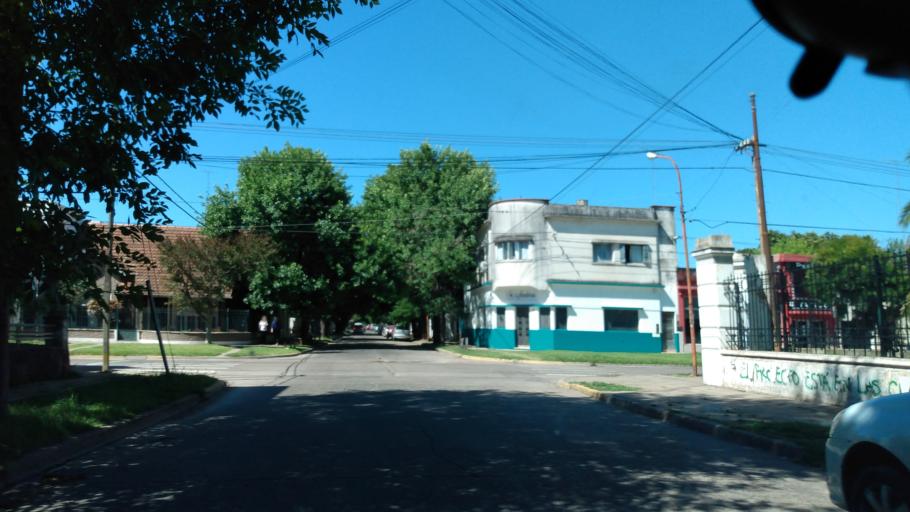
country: AR
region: Buenos Aires
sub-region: Partido de Lujan
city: Lujan
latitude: -34.5671
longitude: -59.1093
